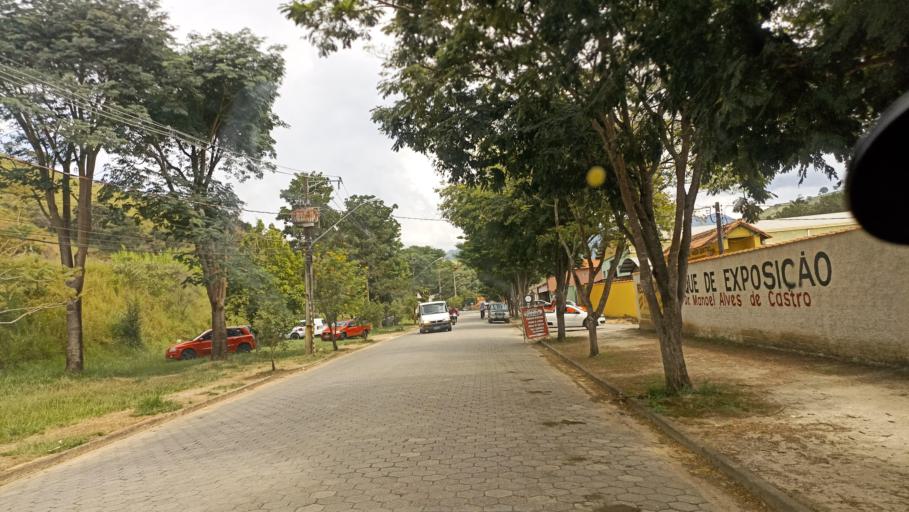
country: BR
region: Minas Gerais
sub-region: Passa Quatro
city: Passa Quatro
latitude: -22.3756
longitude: -44.9625
